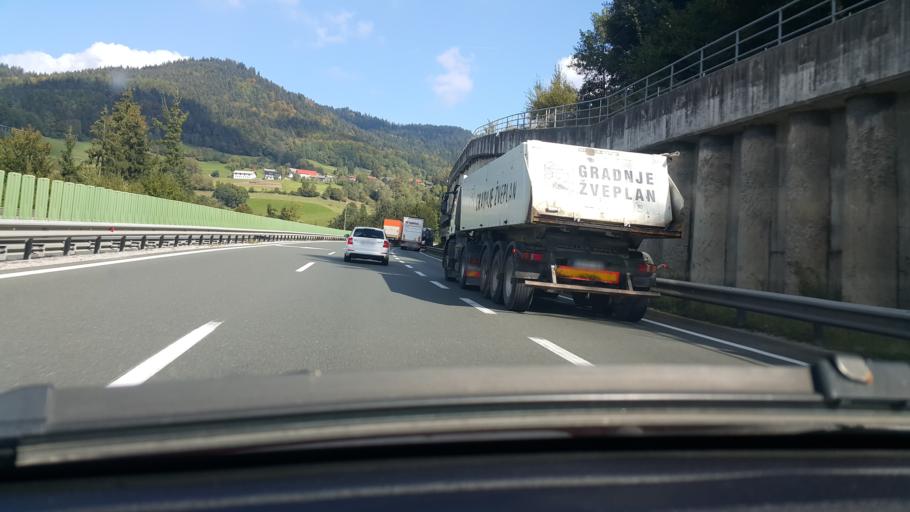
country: SI
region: Moravce
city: Moravce
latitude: 46.1800
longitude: 14.8311
